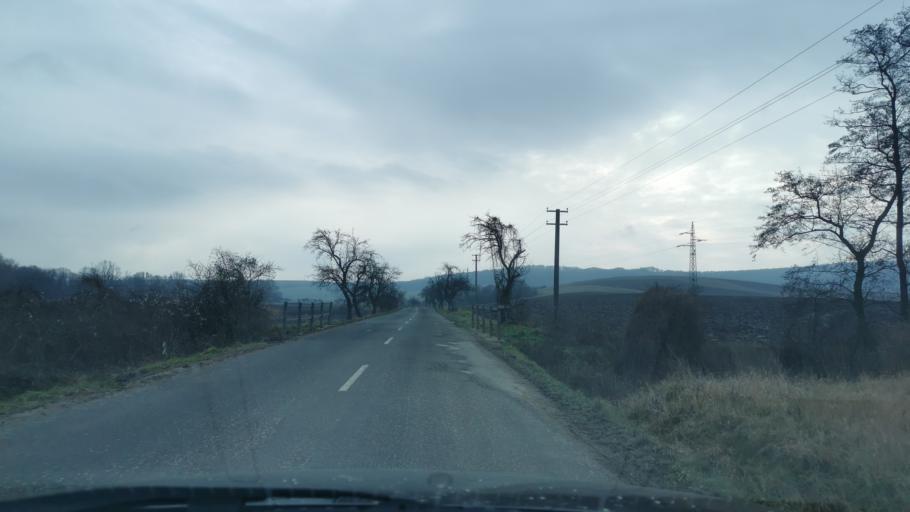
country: SK
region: Trnavsky
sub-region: Okres Skalica
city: Skalica
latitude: 48.7561
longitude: 17.2870
